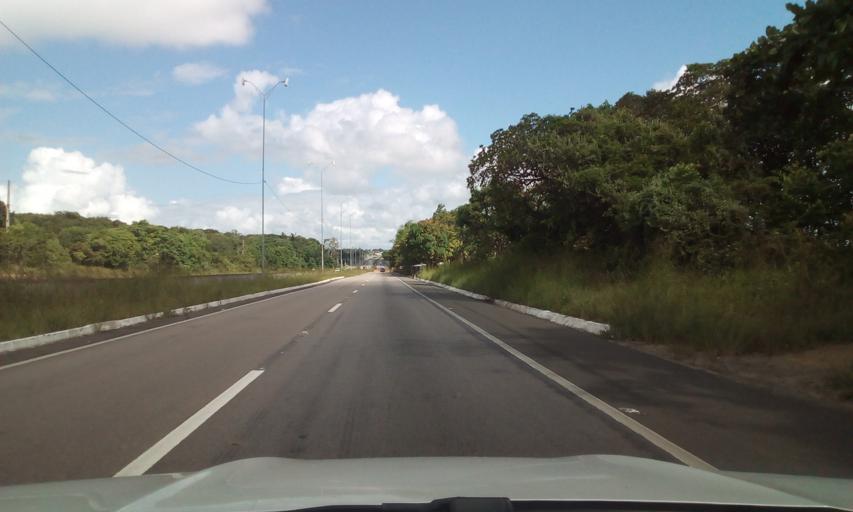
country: BR
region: Paraiba
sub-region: Conde
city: Conde
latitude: -7.3295
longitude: -34.9473
